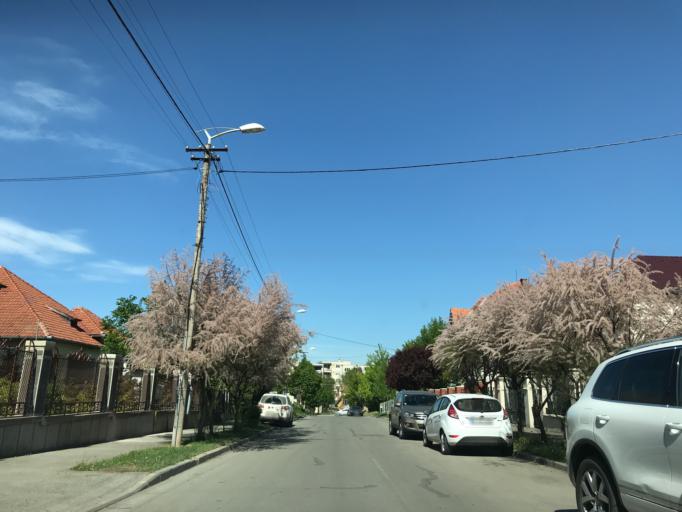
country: RO
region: Cluj
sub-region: Municipiul Cluj-Napoca
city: Cluj-Napoca
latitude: 46.7621
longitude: 23.6027
